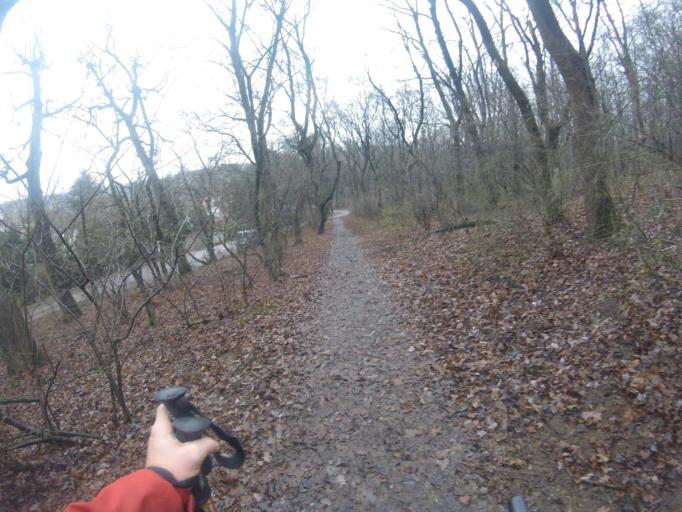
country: HU
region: Pest
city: Budakeszi
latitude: 47.5122
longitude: 18.9387
